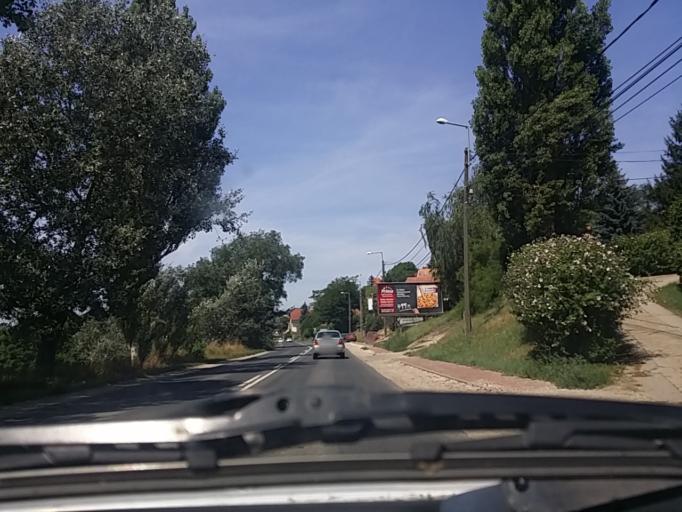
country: HU
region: Pest
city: Pilisborosjeno
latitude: 47.5868
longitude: 18.9953
